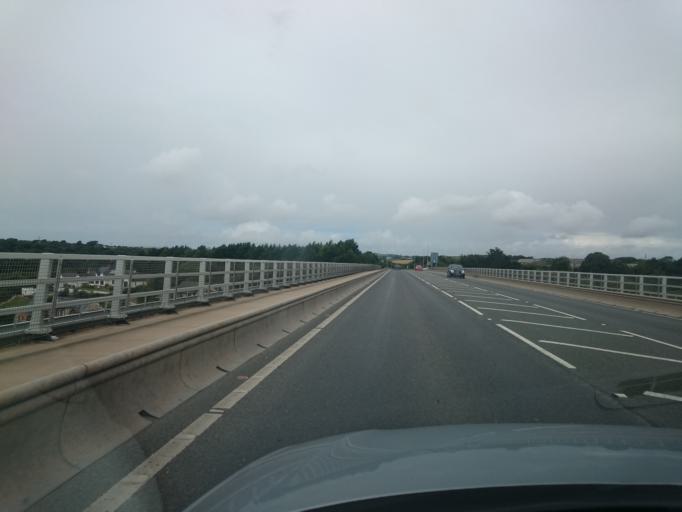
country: GB
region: Wales
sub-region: Pembrokeshire
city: Burton
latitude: 51.7089
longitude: -4.9349
